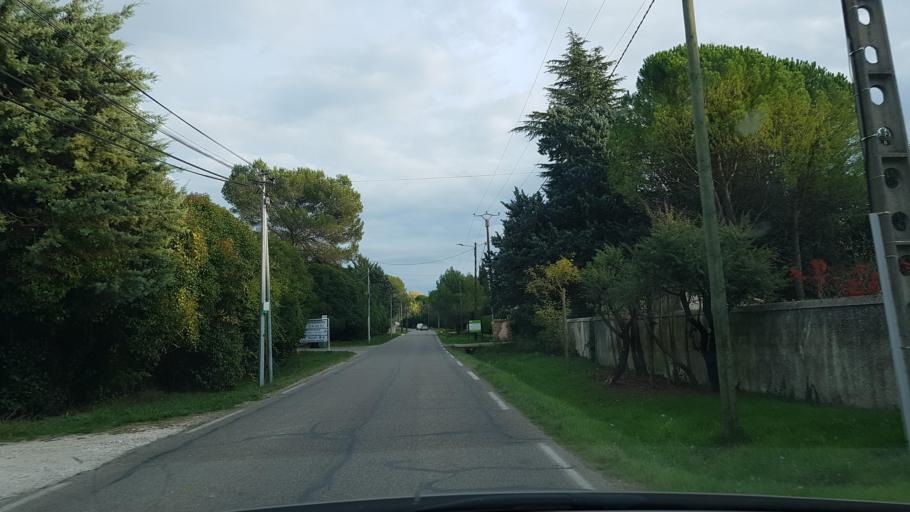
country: FR
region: Provence-Alpes-Cote d'Azur
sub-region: Departement des Bouches-du-Rhone
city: Cabries
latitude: 43.4505
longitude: 5.3624
